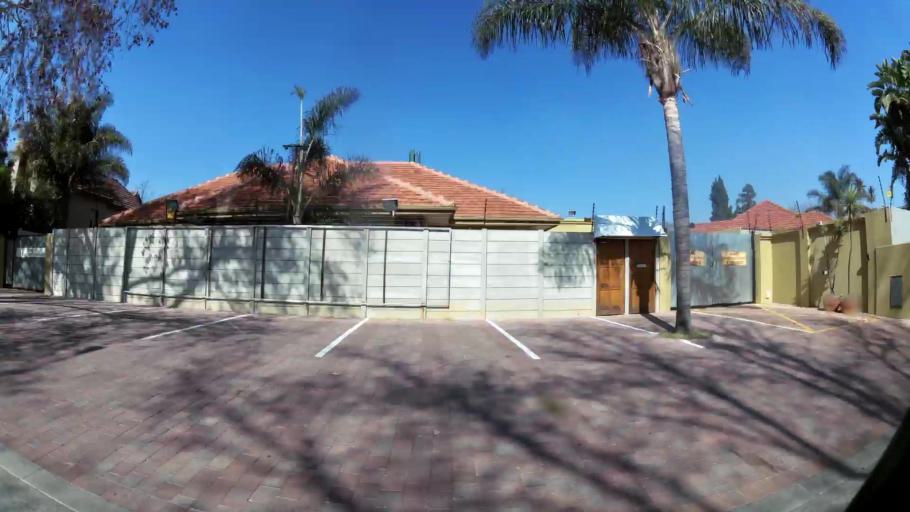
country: ZA
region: Gauteng
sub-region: City of Johannesburg Metropolitan Municipality
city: Johannesburg
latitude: -26.1515
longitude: 28.0106
